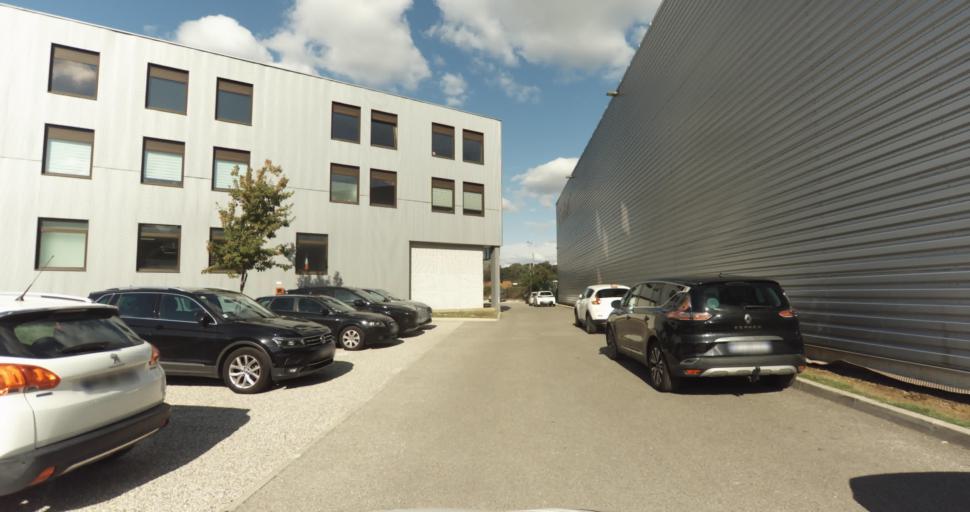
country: FR
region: Rhone-Alpes
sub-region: Departement du Rhone
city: Chaponost
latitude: 45.6982
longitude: 4.7628
